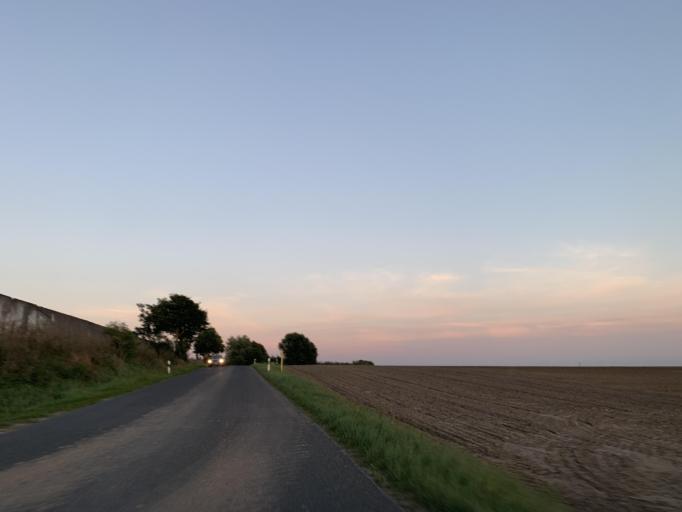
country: DE
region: Mecklenburg-Vorpommern
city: Blankensee
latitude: 53.4474
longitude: 13.2909
